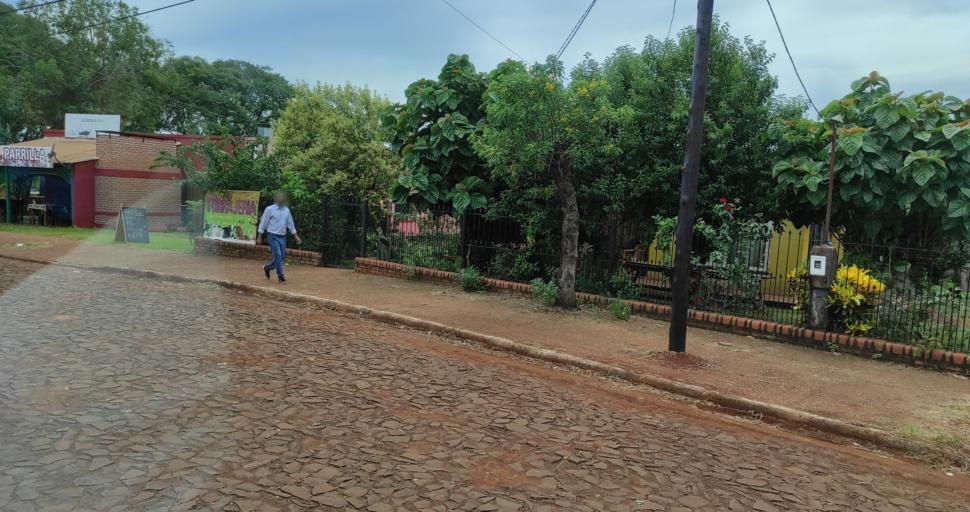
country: AR
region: Misiones
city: El Alcazar
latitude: -26.7175
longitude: -54.8136
